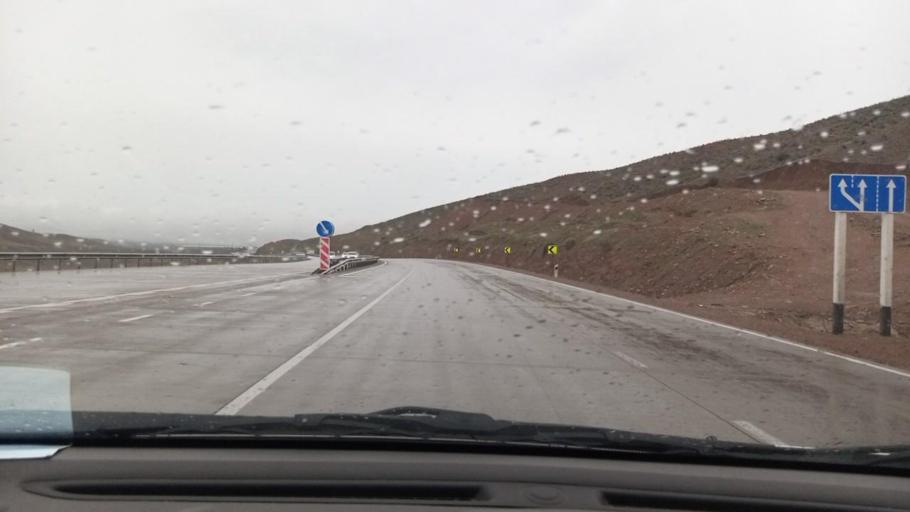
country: UZ
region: Namangan
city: Pop Shahri
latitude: 40.9317
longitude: 70.7024
